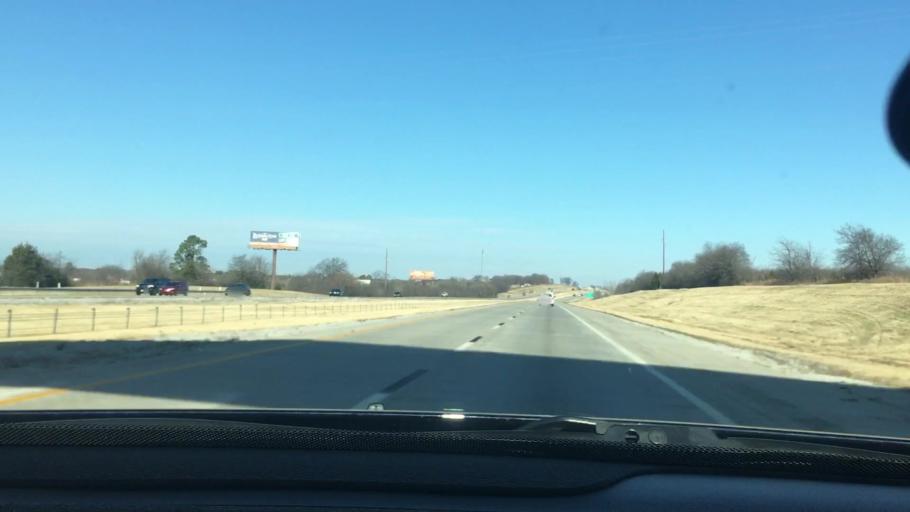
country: US
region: Oklahoma
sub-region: Carter County
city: Ardmore
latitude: 34.1146
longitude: -97.1536
